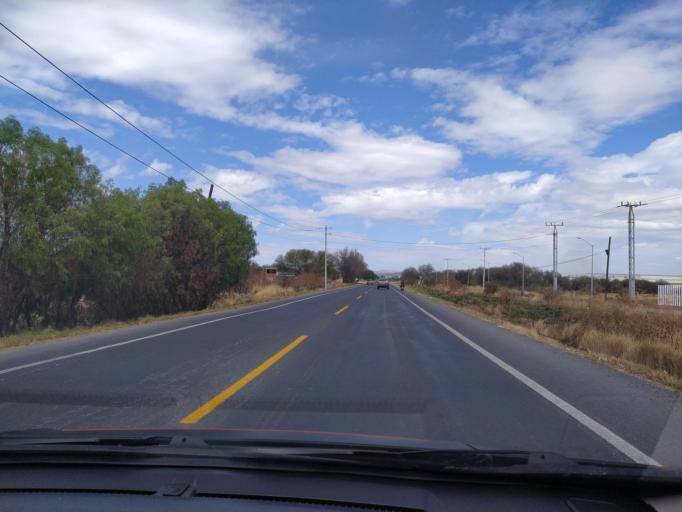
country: LA
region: Oudomxai
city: Muang La
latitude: 20.9994
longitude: 101.8327
